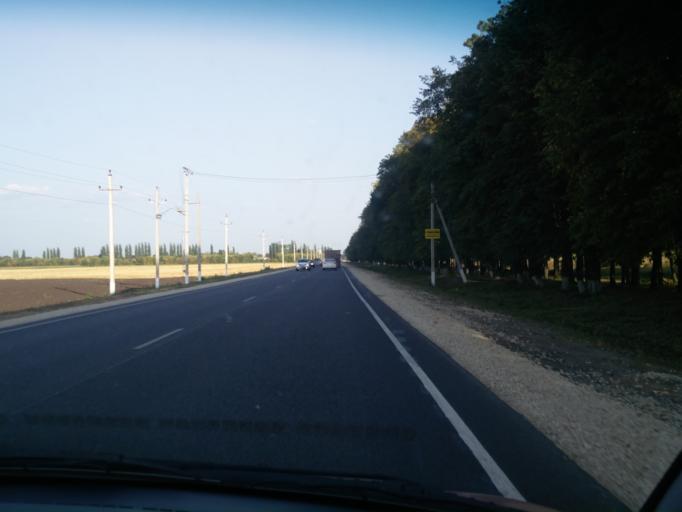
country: RU
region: Voronezj
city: Ramon'
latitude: 51.9219
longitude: 39.2807
